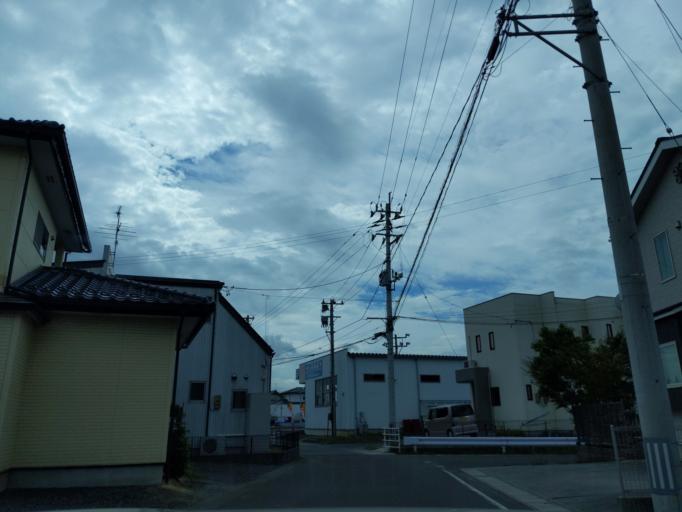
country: JP
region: Fukushima
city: Koriyama
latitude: 37.3987
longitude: 140.4032
